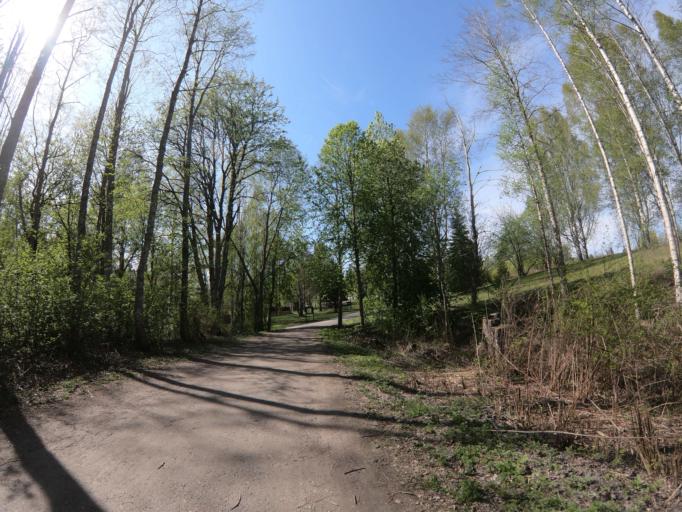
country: SE
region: Vaesterbotten
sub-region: Umea Kommun
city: Roback
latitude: 63.8296
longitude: 20.1761
